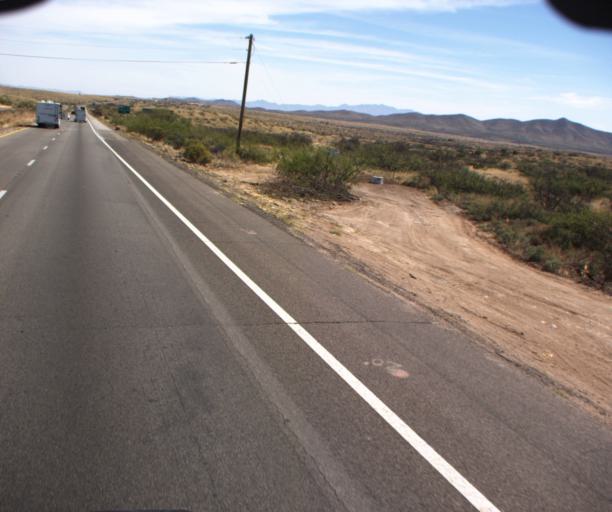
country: US
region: Arizona
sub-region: Cochise County
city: Saint David
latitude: 32.0664
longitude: -110.0707
